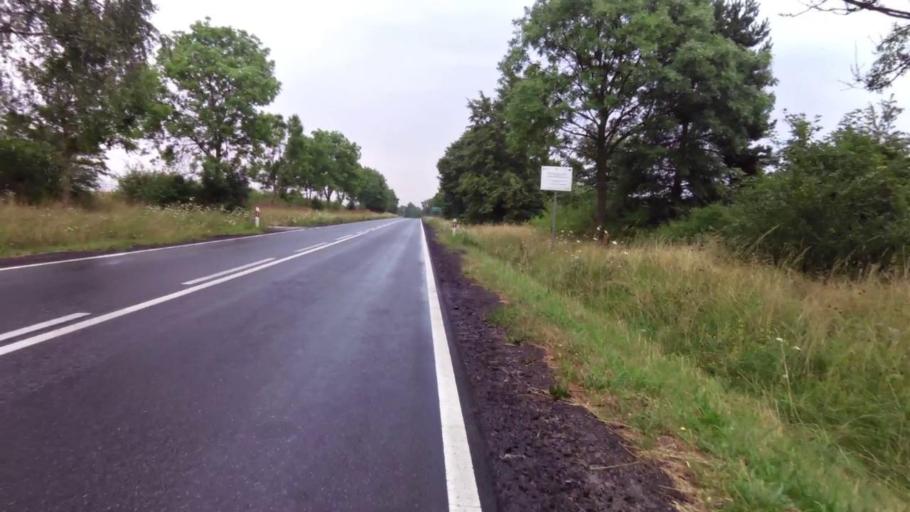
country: PL
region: West Pomeranian Voivodeship
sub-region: Powiat stargardzki
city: Insko
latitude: 53.4490
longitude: 15.5718
